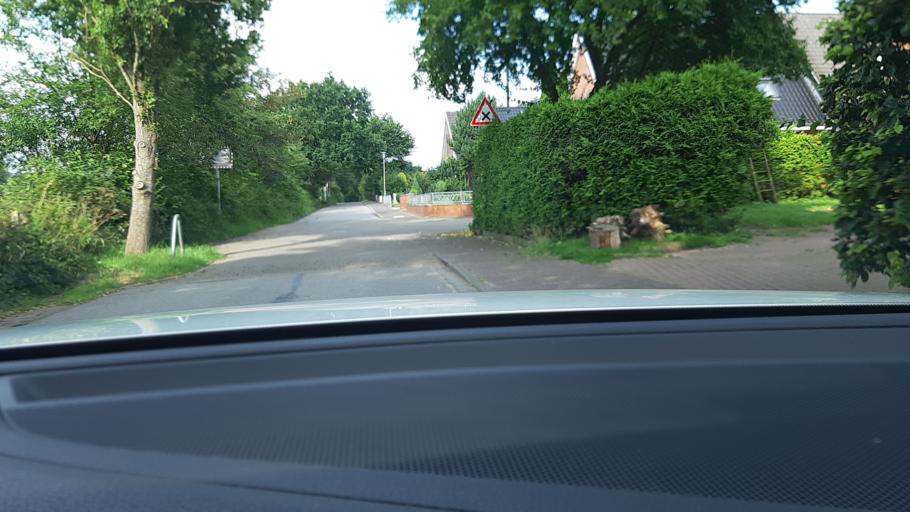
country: DE
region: Schleswig-Holstein
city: Heidekamp
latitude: 53.8552
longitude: 10.5026
